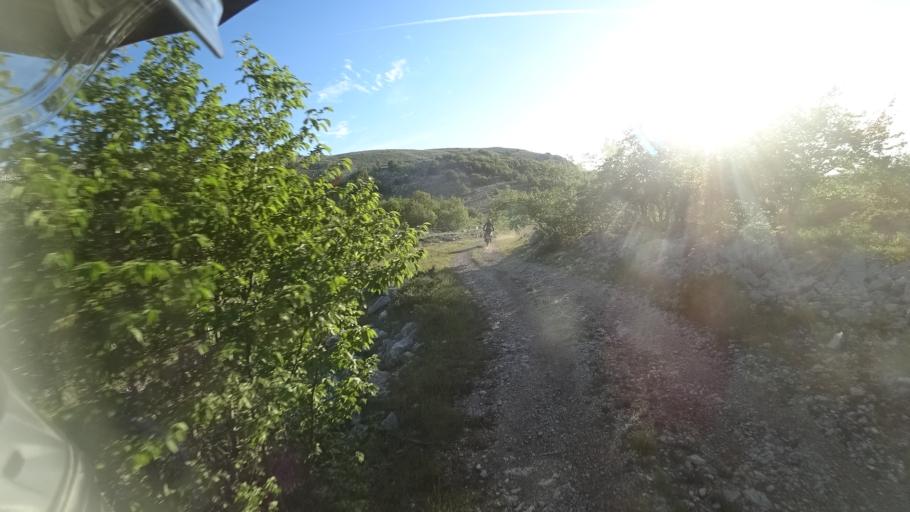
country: HR
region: Sibensko-Kniniska
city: Drnis
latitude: 43.8705
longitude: 16.3701
